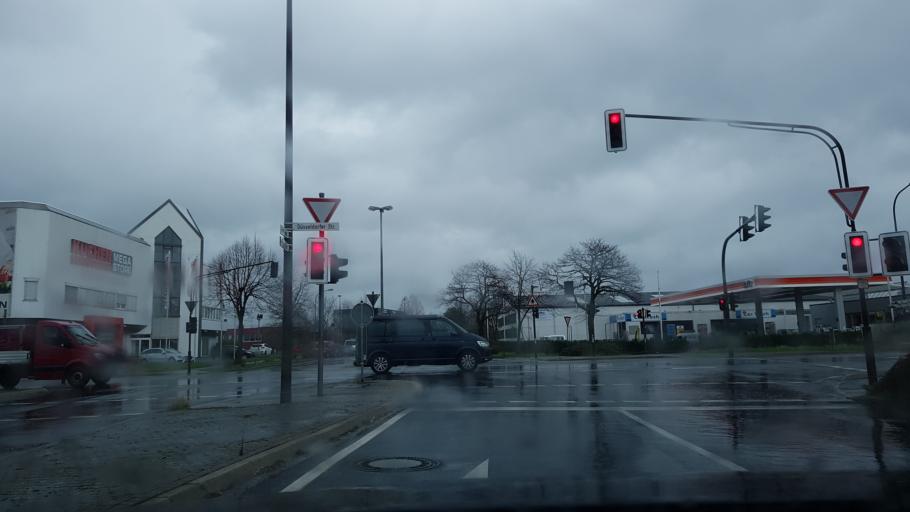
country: DE
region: North Rhine-Westphalia
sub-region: Regierungsbezirk Dusseldorf
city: Langenfeld
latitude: 51.1219
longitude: 6.9238
